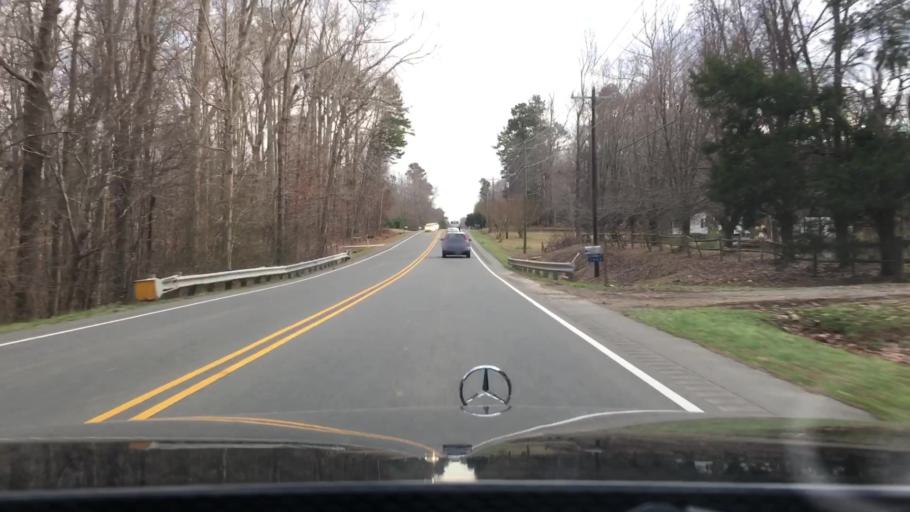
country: US
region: North Carolina
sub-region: Orange County
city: Hillsborough
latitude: 36.1159
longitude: -79.1130
